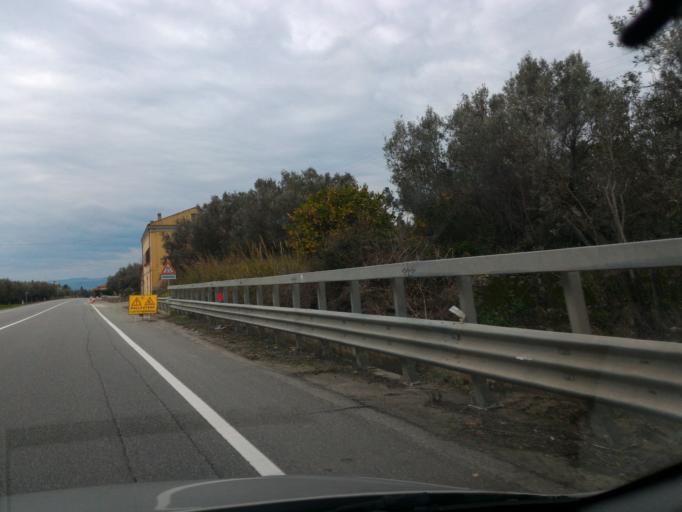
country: IT
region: Calabria
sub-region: Provincia di Catanzaro
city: Barone
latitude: 38.8498
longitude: 16.6636
